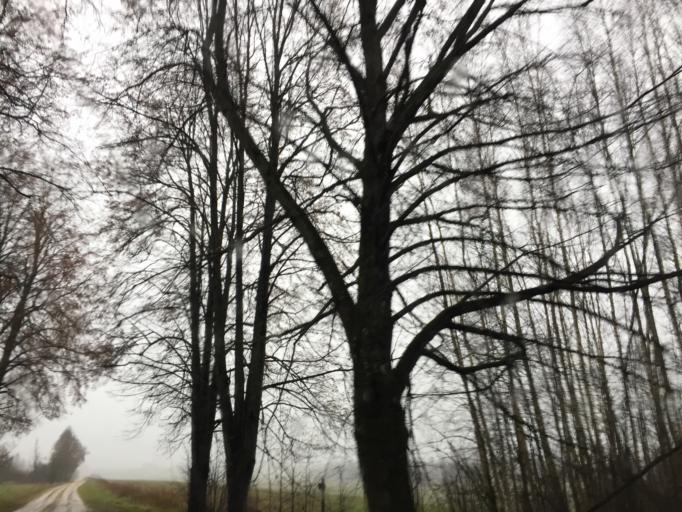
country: LV
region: Viesite
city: Viesite
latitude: 56.4569
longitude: 25.6275
